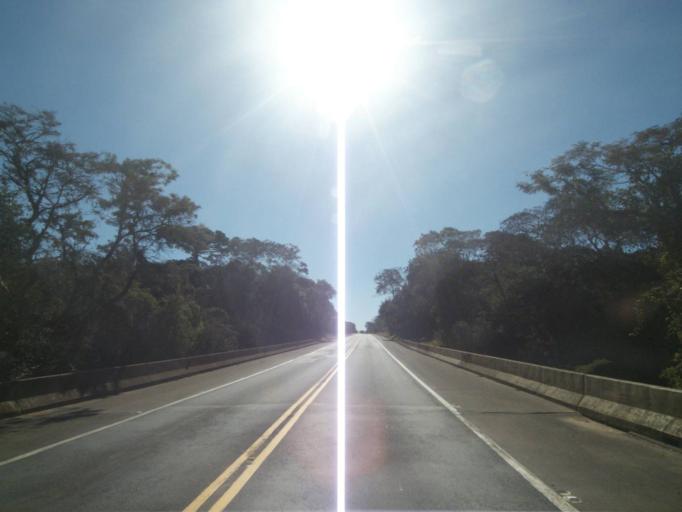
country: BR
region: Parana
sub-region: Tibagi
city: Tibagi
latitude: -24.7394
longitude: -50.5375
